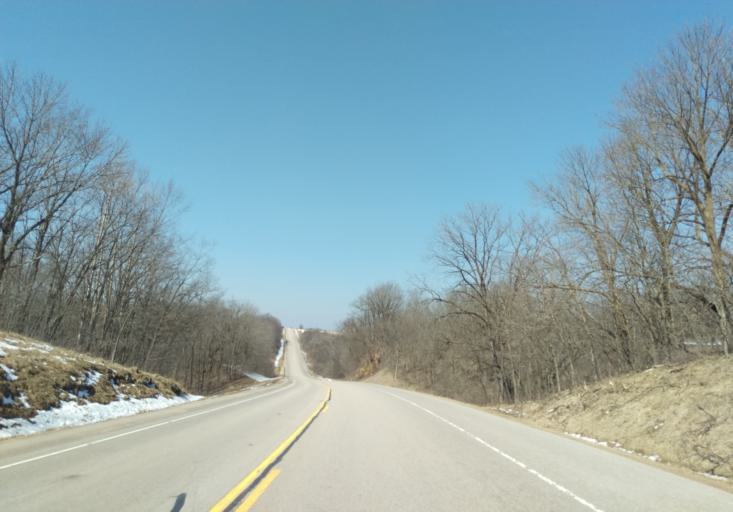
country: US
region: Wisconsin
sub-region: Richland County
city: Richland Center
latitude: 43.4107
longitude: -90.6303
